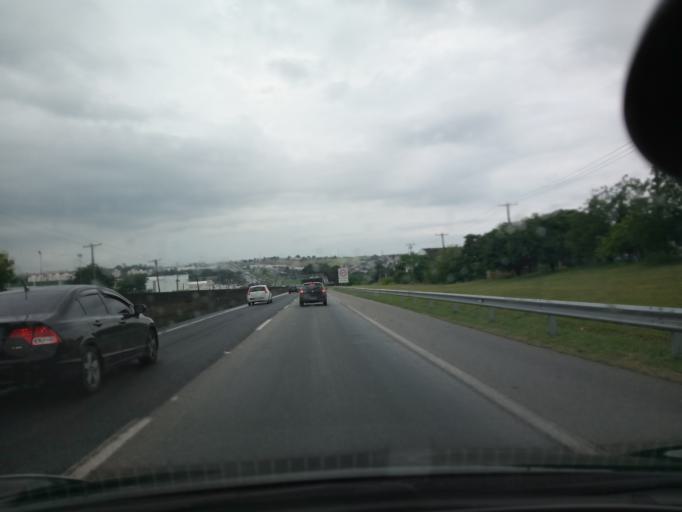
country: BR
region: Sao Paulo
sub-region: Campinas
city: Campinas
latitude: -22.9601
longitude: -47.0966
